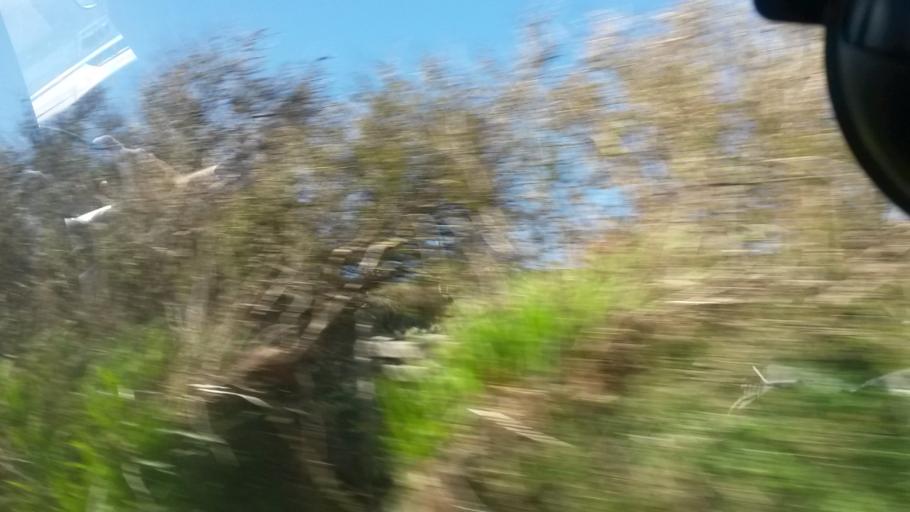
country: IE
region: Munster
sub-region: Ciarrai
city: Dingle
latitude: 52.1357
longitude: -10.4539
